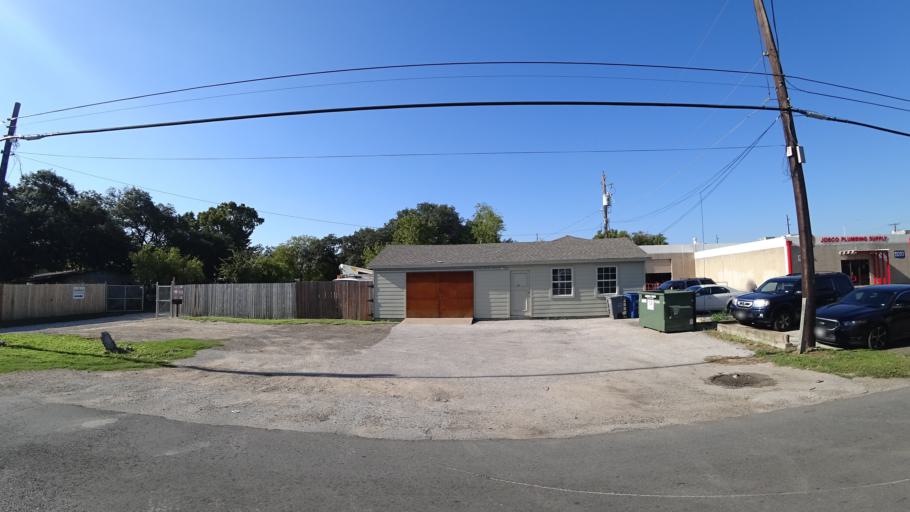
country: US
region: Texas
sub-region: Travis County
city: Austin
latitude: 30.3503
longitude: -97.7082
